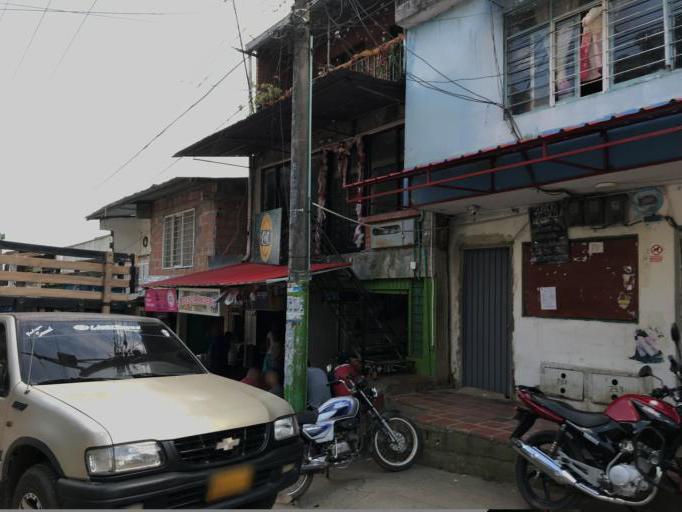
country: CO
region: Valle del Cauca
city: Cali
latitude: 3.4675
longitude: -76.6302
